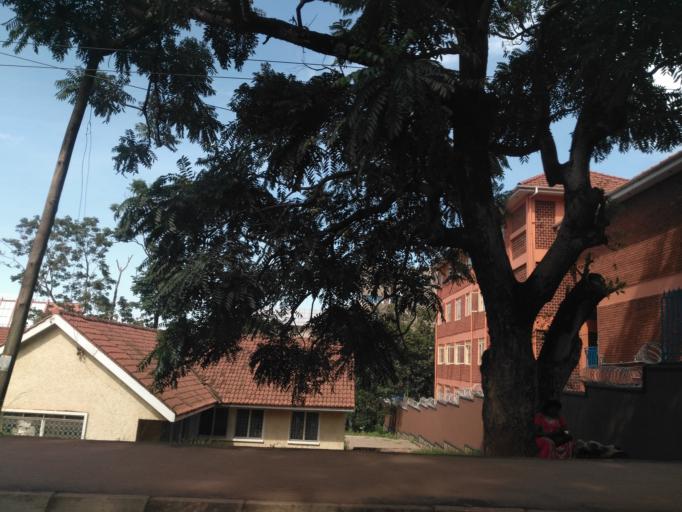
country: UG
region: Central Region
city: Kampala Central Division
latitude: 0.3274
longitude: 32.5750
